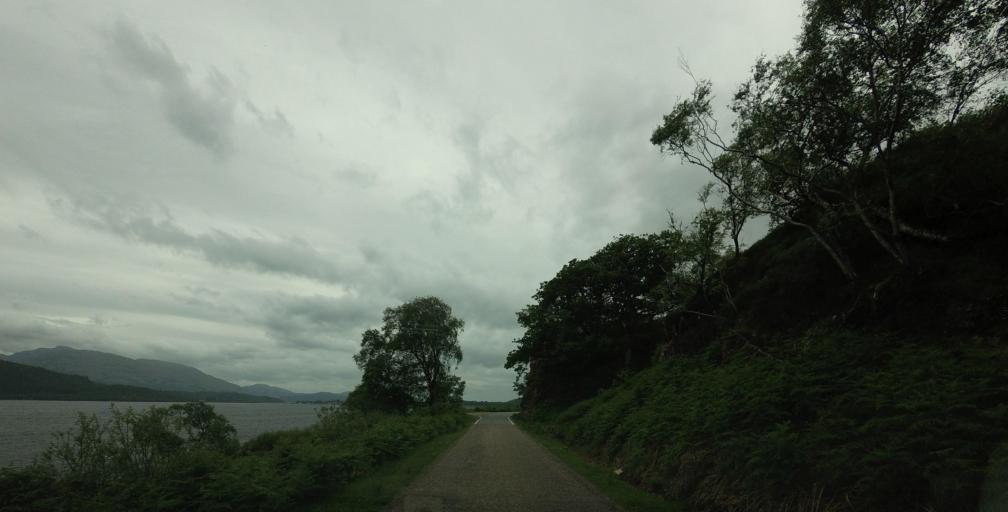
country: GB
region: Scotland
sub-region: Highland
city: Fort William
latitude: 56.7501
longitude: -5.2331
